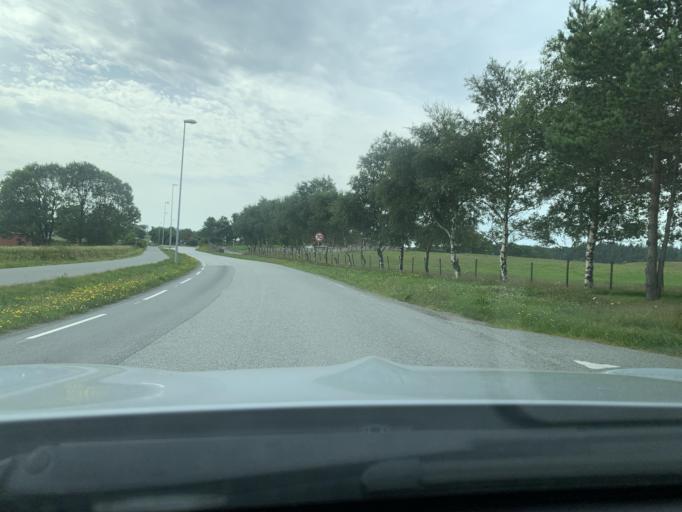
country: NO
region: Rogaland
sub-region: Time
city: Bryne
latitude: 58.7613
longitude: 5.7099
